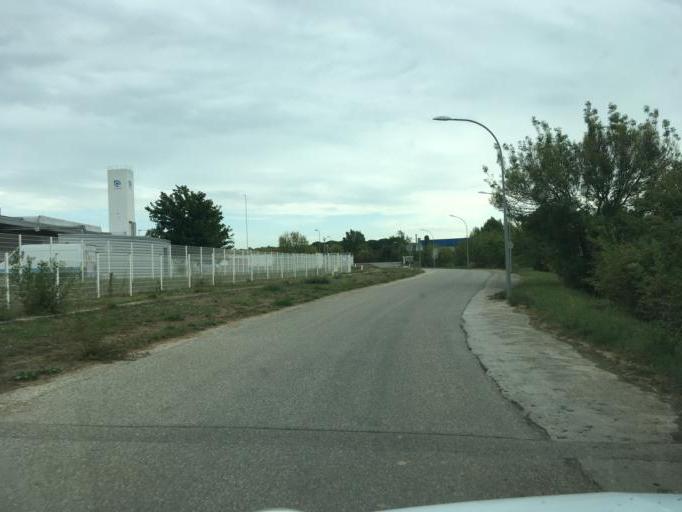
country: FR
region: Provence-Alpes-Cote d'Azur
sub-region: Departement des Bouches-du-Rhone
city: Rousset
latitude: 43.4728
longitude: 5.6016
